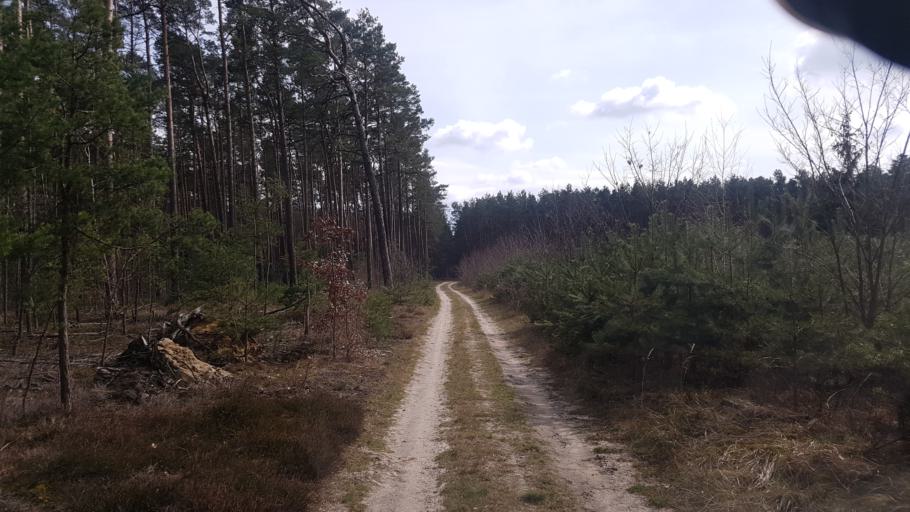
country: DE
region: Brandenburg
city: Schonborn
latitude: 51.6818
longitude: 13.4668
